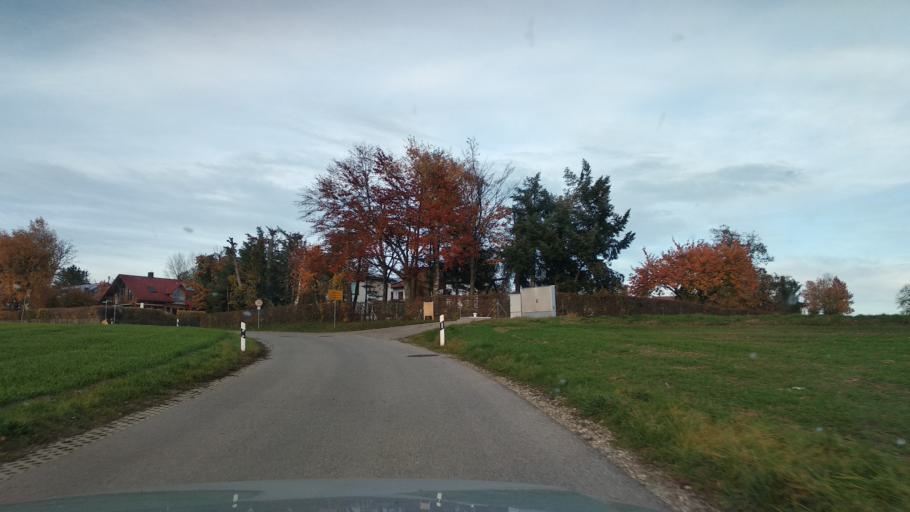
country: DE
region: Bavaria
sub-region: Upper Bavaria
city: Grafing bei Munchen
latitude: 48.0327
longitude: 11.9873
